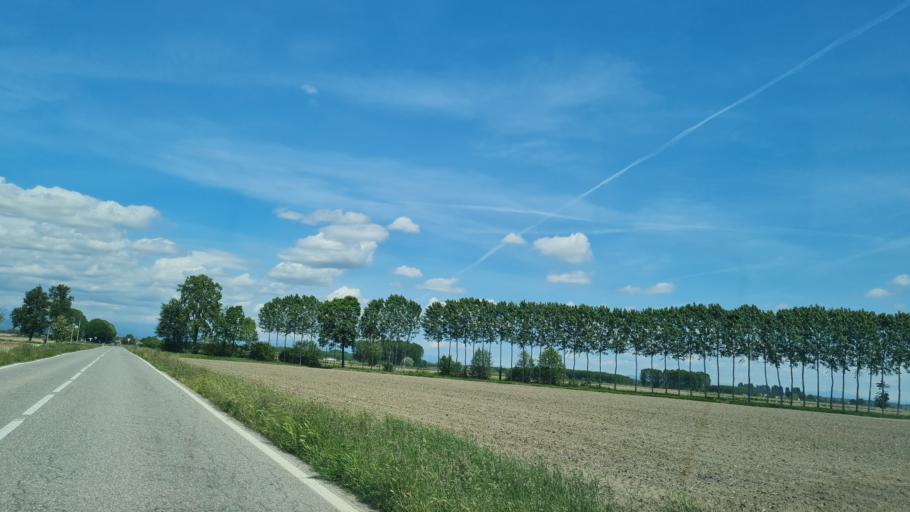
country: IT
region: Piedmont
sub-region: Provincia di Novara
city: Sillavengo
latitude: 45.5047
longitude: 8.4435
